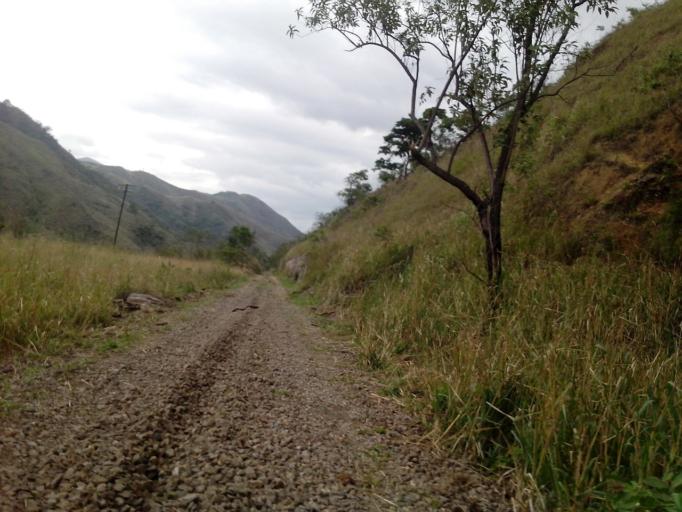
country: BR
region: Rio de Janeiro
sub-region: Miguel Pereira
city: Miguel Pereira
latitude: -22.5033
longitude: -43.5035
